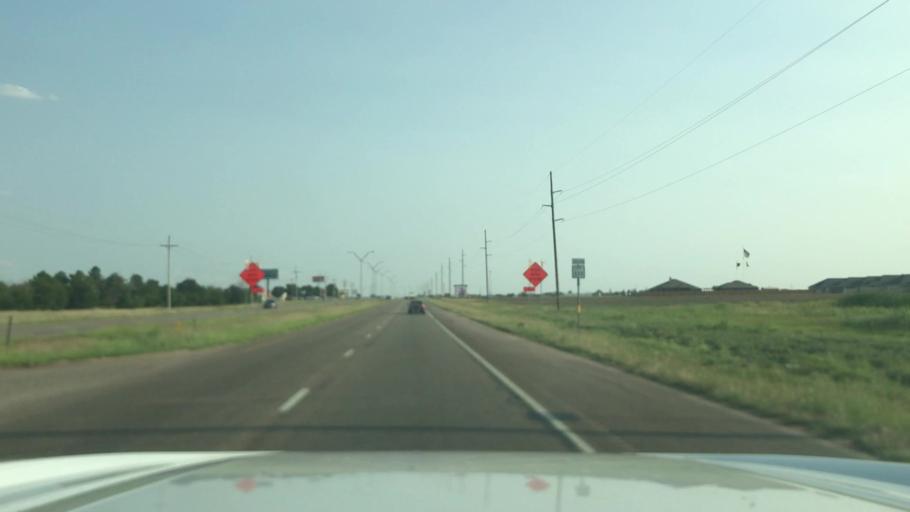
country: US
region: Texas
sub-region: Potter County
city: Bushland
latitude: 35.1297
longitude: -101.9382
